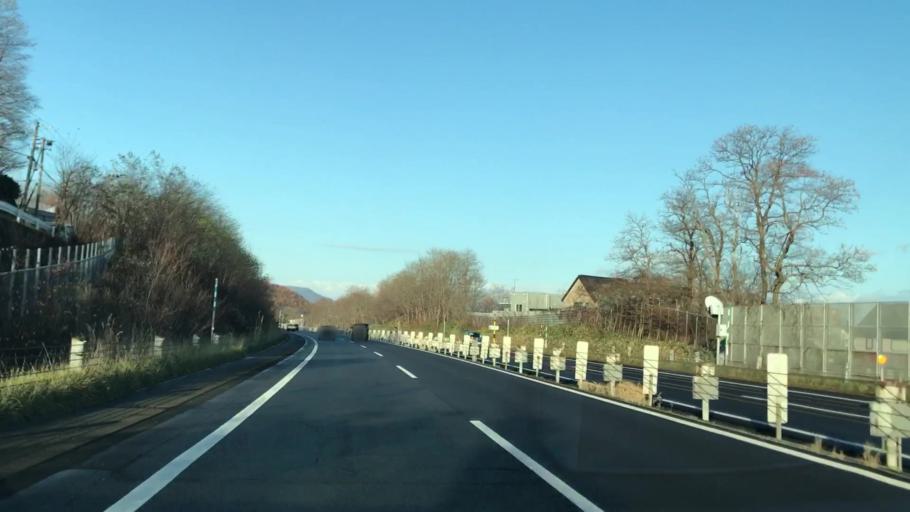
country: JP
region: Hokkaido
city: Sapporo
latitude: 43.1180
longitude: 141.2299
